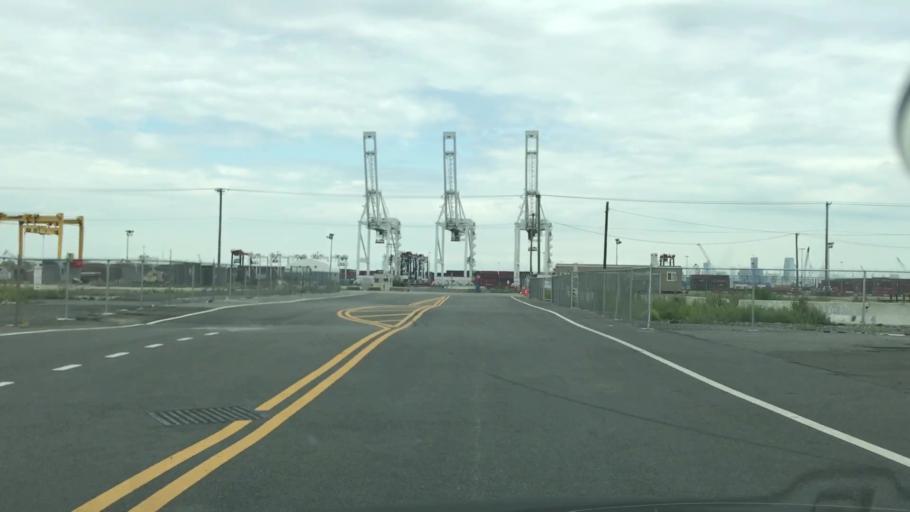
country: US
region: New Jersey
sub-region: Hudson County
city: Bayonne
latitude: 40.6683
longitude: -74.0866
